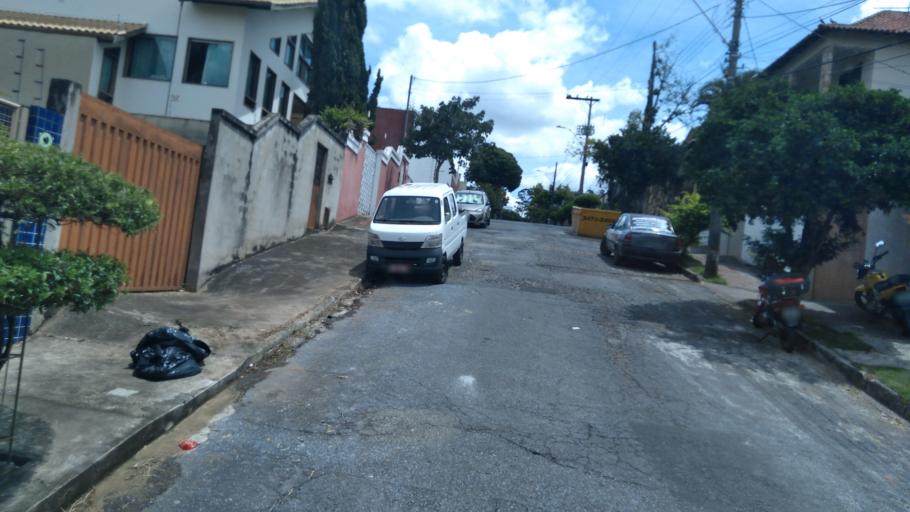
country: BR
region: Minas Gerais
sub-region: Contagem
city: Contagem
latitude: -19.9151
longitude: -44.0065
